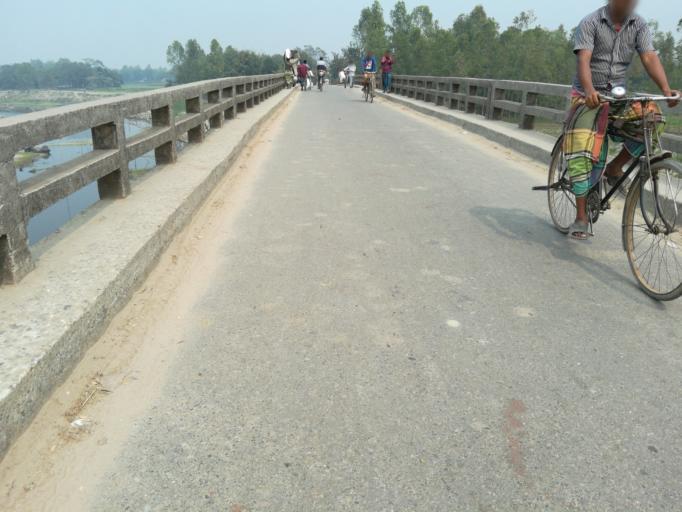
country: BD
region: Dhaka
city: Nagarpur
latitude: 23.9008
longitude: 89.8739
